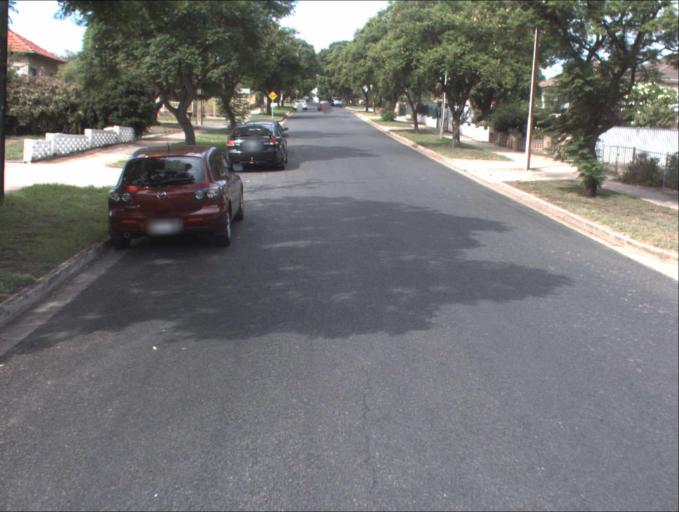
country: AU
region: South Australia
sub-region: Port Adelaide Enfield
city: Blair Athol
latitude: -34.8639
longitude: 138.5946
